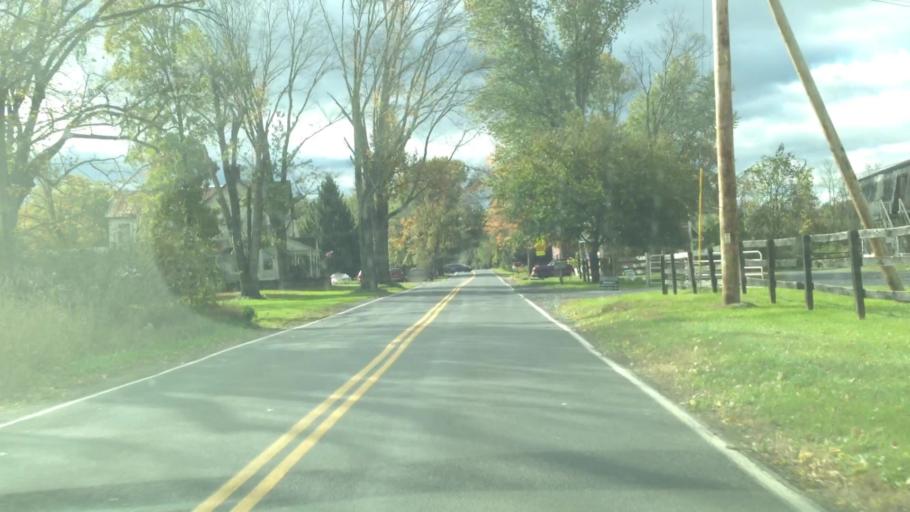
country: US
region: New York
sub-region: Ulster County
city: New Paltz
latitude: 41.7790
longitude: -74.0893
